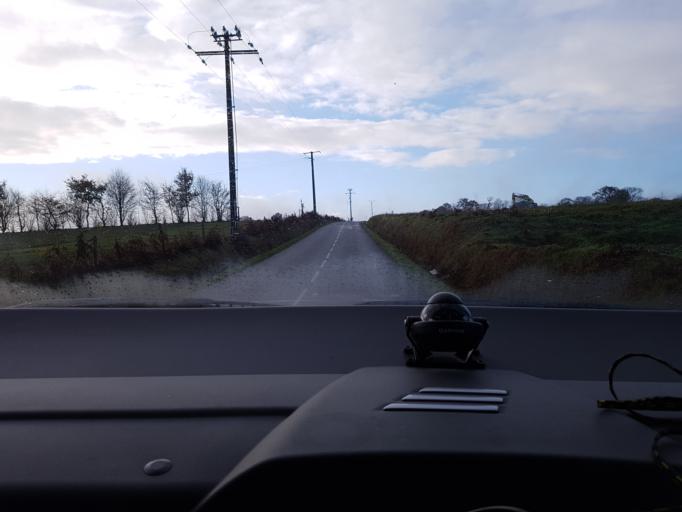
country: FR
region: Brittany
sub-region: Departement d'Ille-et-Vilaine
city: La Bouexiere
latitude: 48.1893
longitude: -1.4241
